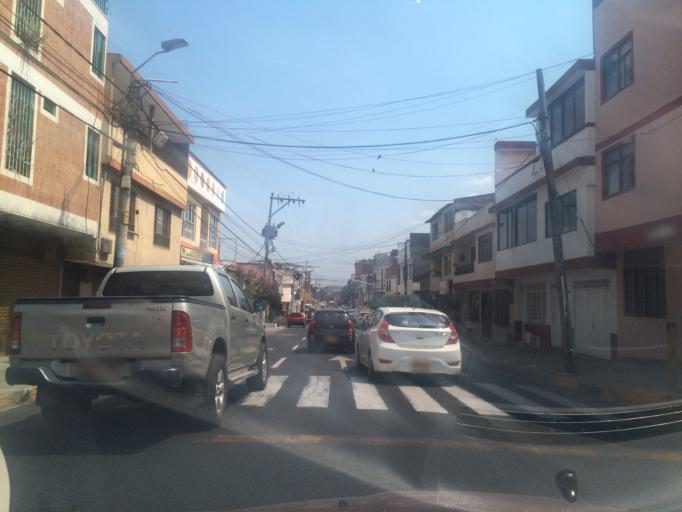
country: CO
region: Valle del Cauca
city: Cali
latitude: 3.4373
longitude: -76.5353
